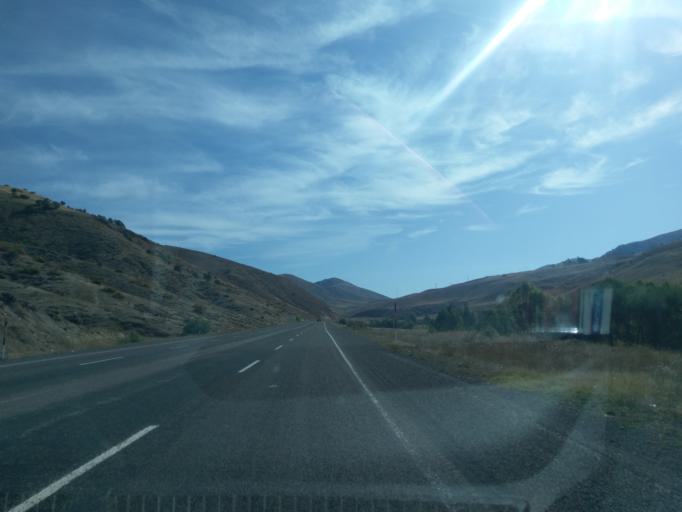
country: TR
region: Sivas
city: Akincilar
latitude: 39.8625
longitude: 38.3339
